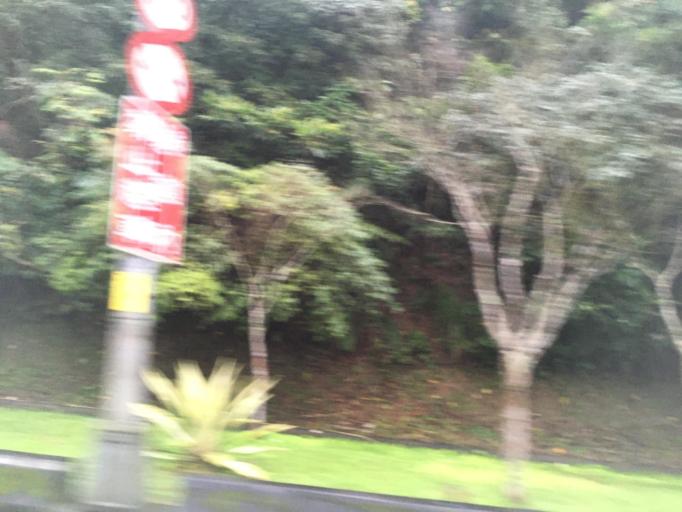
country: TW
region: Taiwan
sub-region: Keelung
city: Keelung
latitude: 25.0192
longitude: 121.7940
